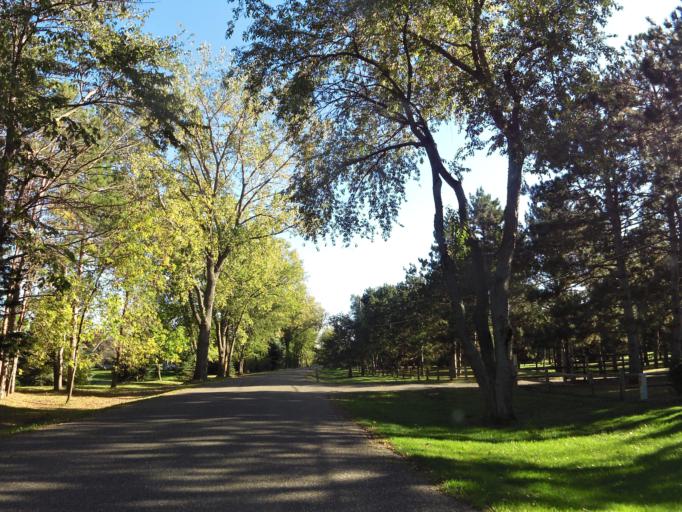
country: US
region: Minnesota
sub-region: Washington County
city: Lakeland
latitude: 44.9509
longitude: -92.7414
